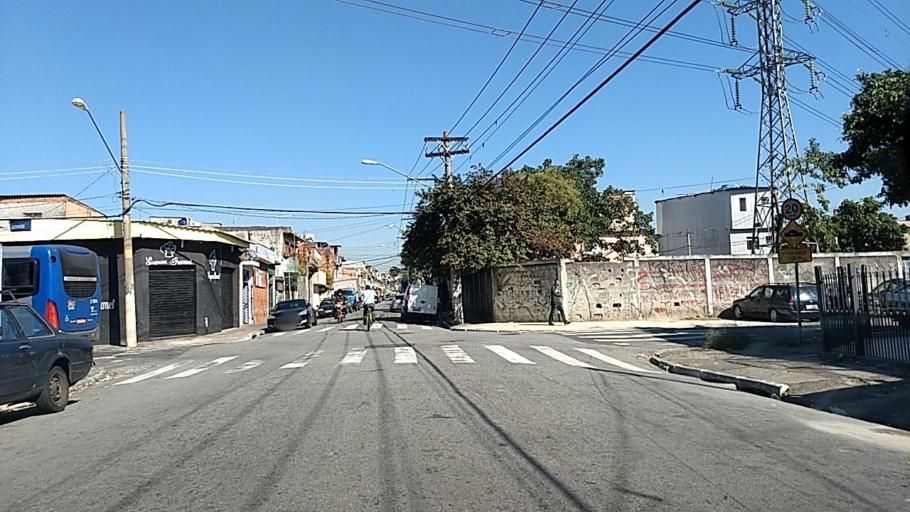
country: BR
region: Sao Paulo
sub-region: Guarulhos
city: Guarulhos
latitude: -23.4834
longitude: -46.5677
